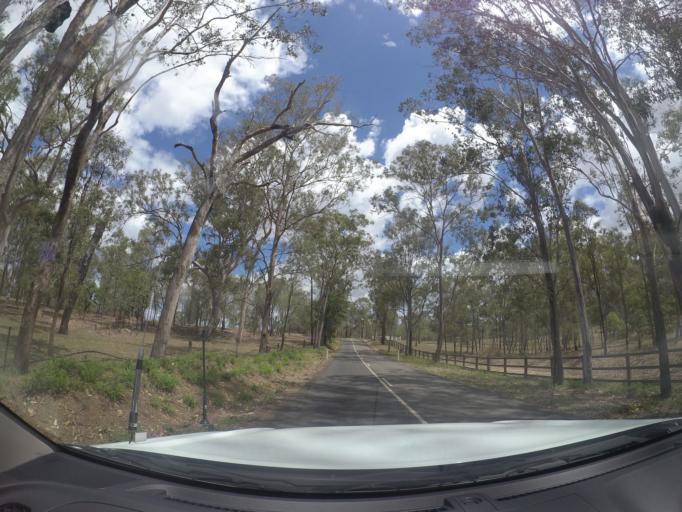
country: AU
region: Queensland
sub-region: Logan
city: Cedar Vale
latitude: -27.9377
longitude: 153.0687
